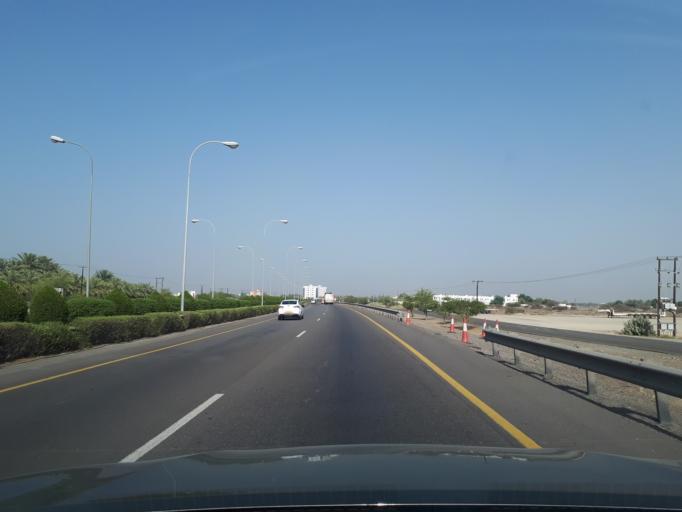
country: OM
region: Al Batinah
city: Al Sohar
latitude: 24.4118
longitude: 56.6374
